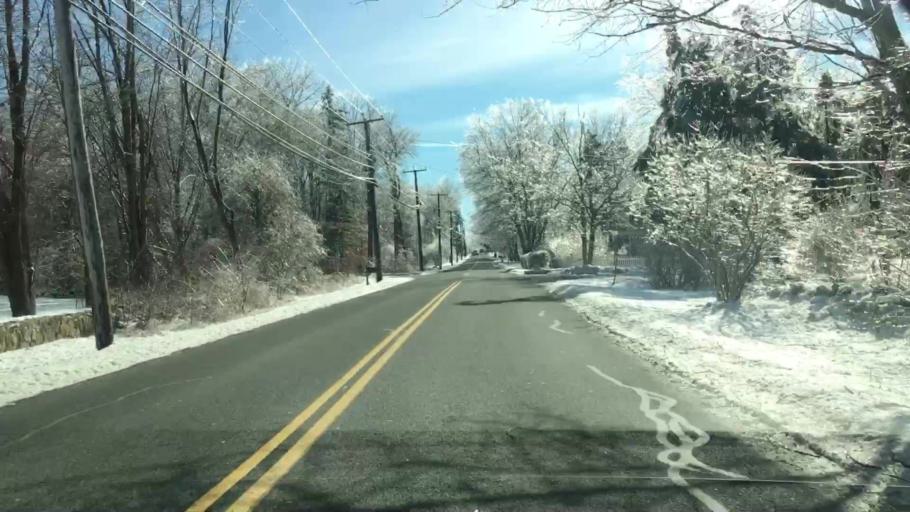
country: US
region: Connecticut
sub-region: Fairfield County
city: Trumbull
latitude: 41.3287
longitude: -73.2221
